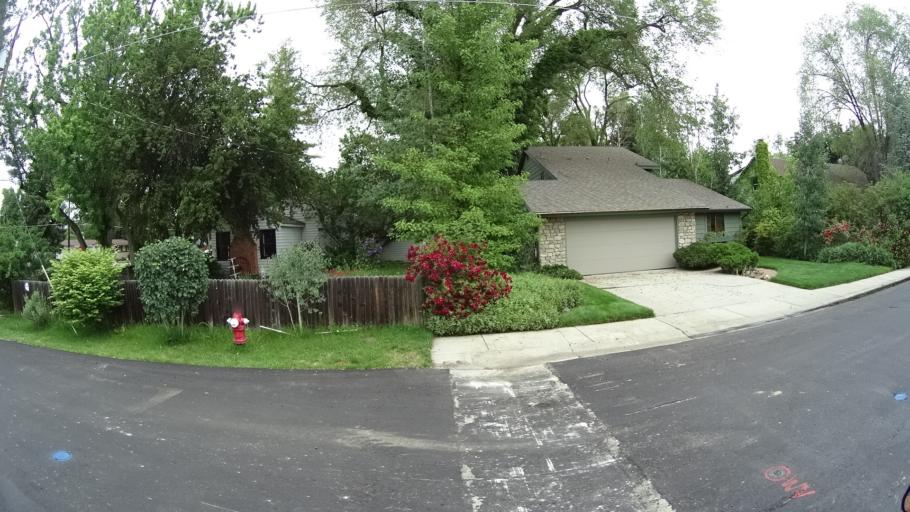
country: US
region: Idaho
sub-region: Ada County
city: Boise
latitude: 43.5787
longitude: -116.2038
